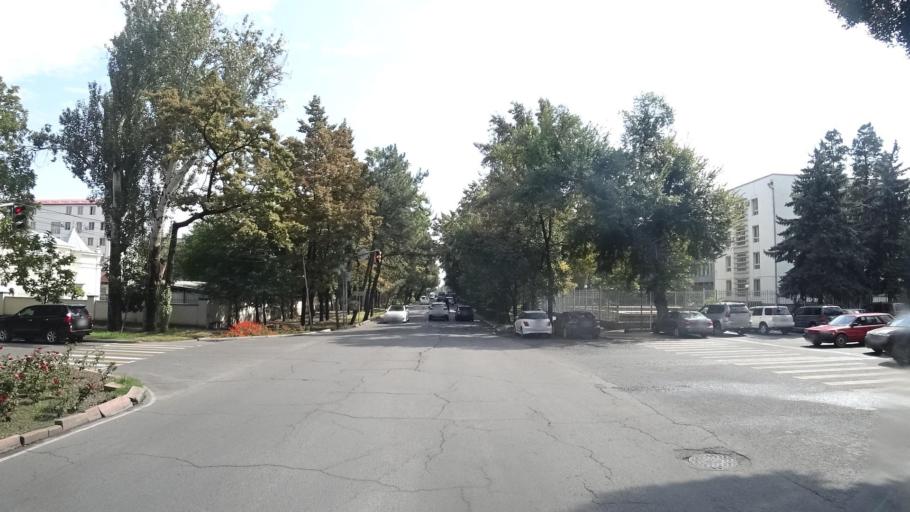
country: KG
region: Chuy
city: Bishkek
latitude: 42.8806
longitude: 74.6071
